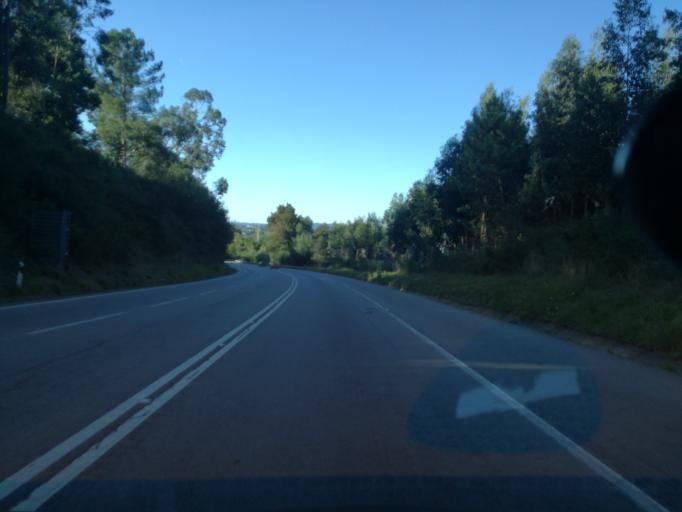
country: PT
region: Porto
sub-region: Santo Tirso
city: Sao Miguel do Couto
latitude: 41.3223
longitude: -8.4689
